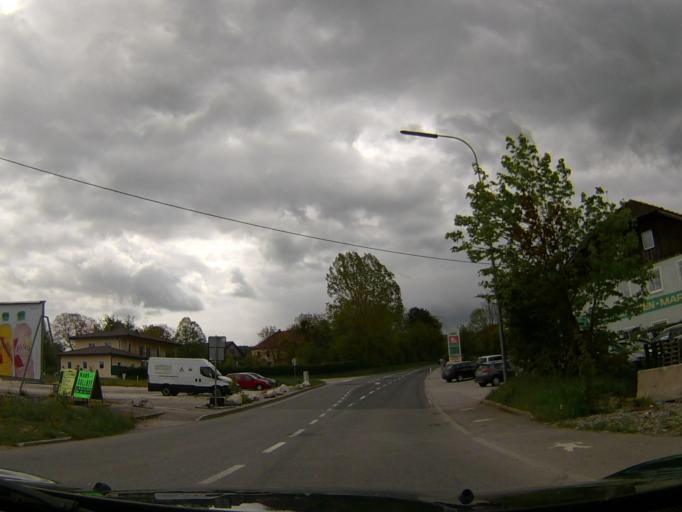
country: AT
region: Upper Austria
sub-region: Politischer Bezirk Vocklabruck
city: Seewalchen
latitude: 47.9448
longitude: 13.5948
